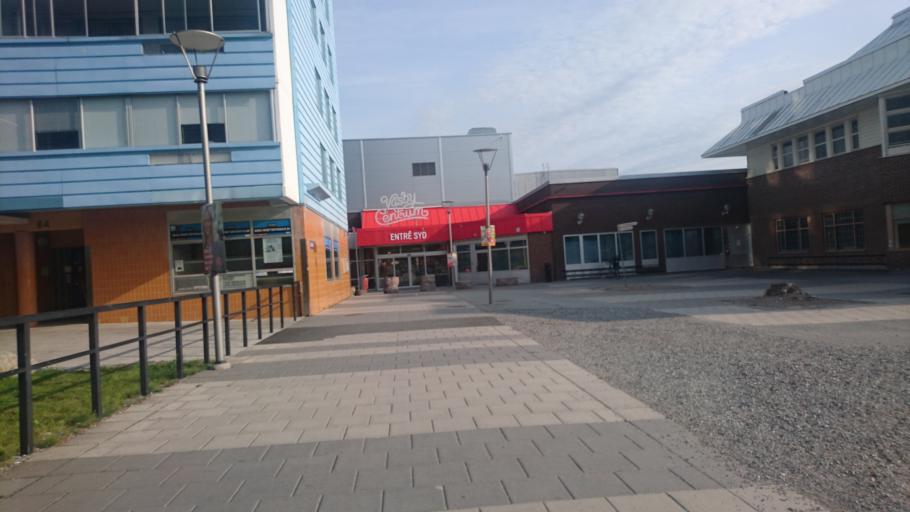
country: SE
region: Stockholm
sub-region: Upplands Vasby Kommun
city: Upplands Vaesby
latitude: 59.5165
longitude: 17.9116
